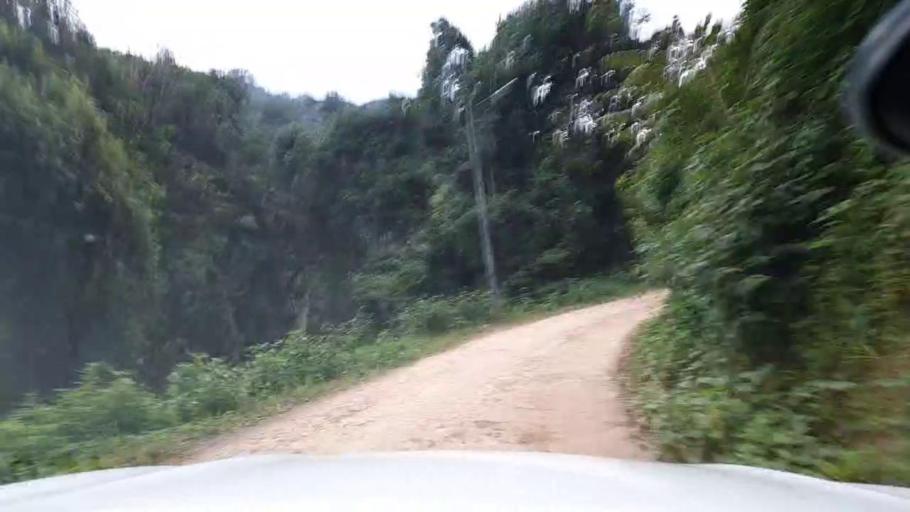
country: RW
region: Southern Province
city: Nzega
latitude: -2.5548
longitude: 29.2338
